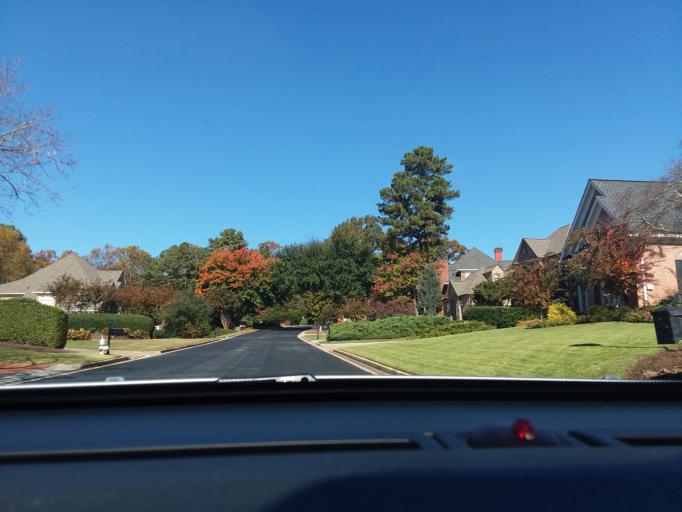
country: US
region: Georgia
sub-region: Fulton County
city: Johns Creek
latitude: 34.0255
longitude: -84.1836
